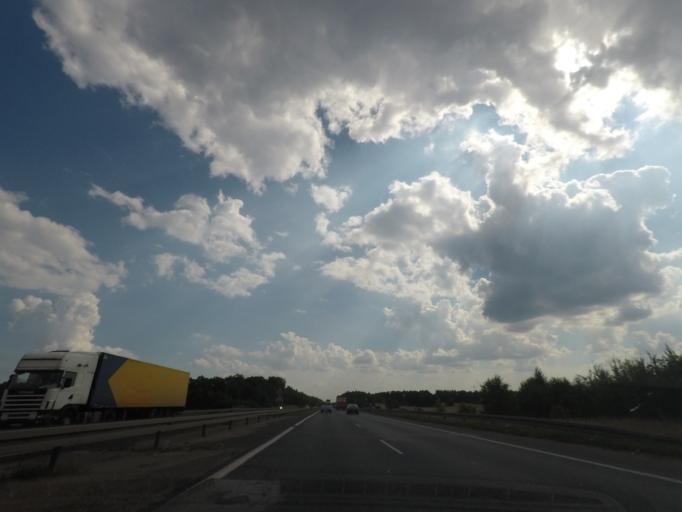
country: PL
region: Lodz Voivodeship
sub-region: Powiat radomszczanski
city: Radomsko
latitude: 51.0776
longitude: 19.3709
